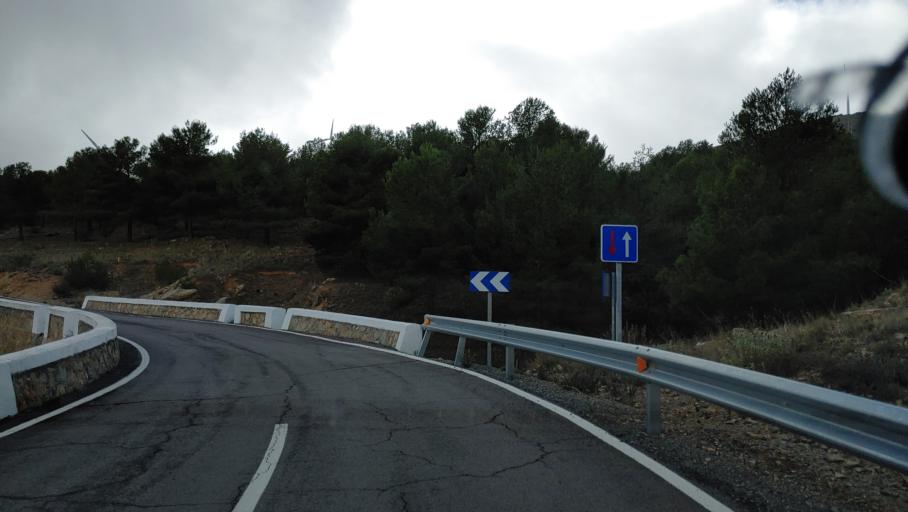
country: ES
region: Andalusia
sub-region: Provincia de Almeria
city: Enix
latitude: 36.9037
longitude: -2.6118
